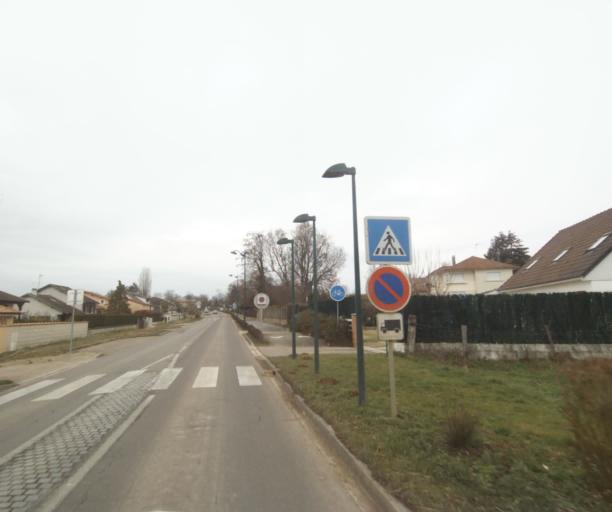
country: FR
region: Champagne-Ardenne
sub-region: Departement de la Haute-Marne
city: Villiers-en-Lieu
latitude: 48.6628
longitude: 4.9068
